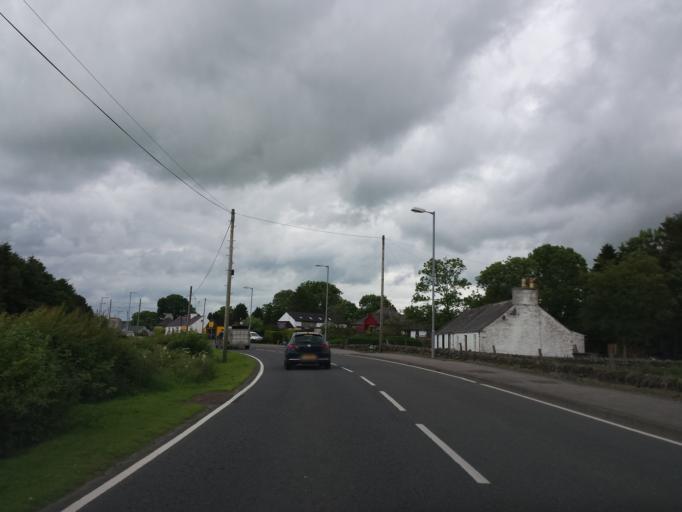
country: GB
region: Scotland
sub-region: Dumfries and Galloway
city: Dalbeattie
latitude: 55.0075
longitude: -3.8680
